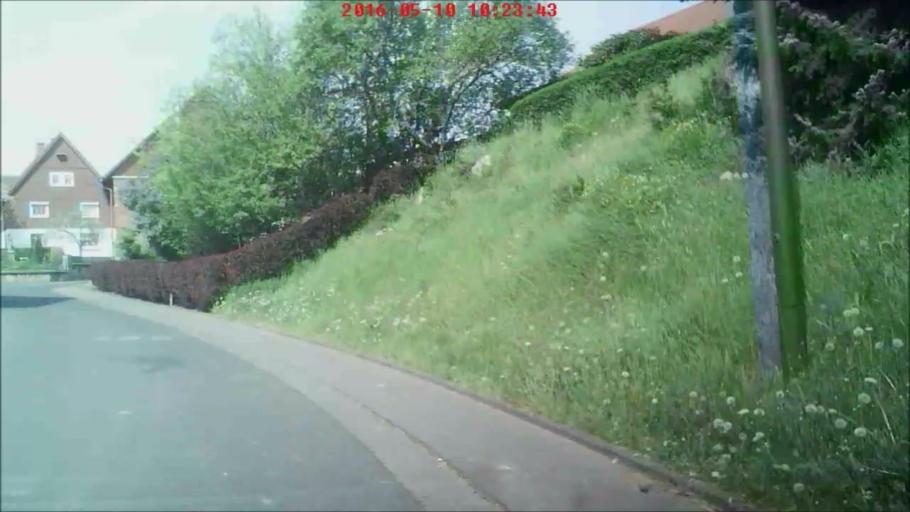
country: DE
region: Hesse
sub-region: Regierungsbezirk Kassel
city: Dipperz
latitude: 50.5441
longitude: 9.7575
